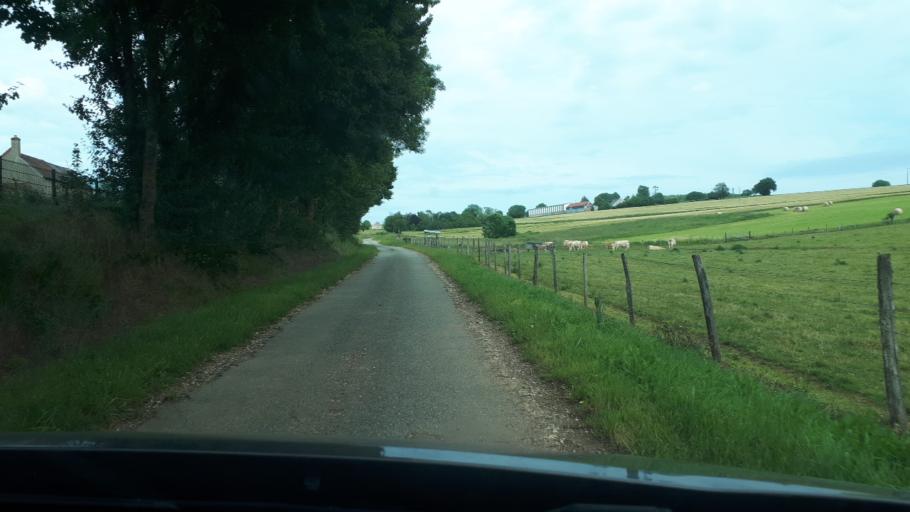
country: FR
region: Centre
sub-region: Departement du Cher
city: Sancerre
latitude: 47.3182
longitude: 2.7315
